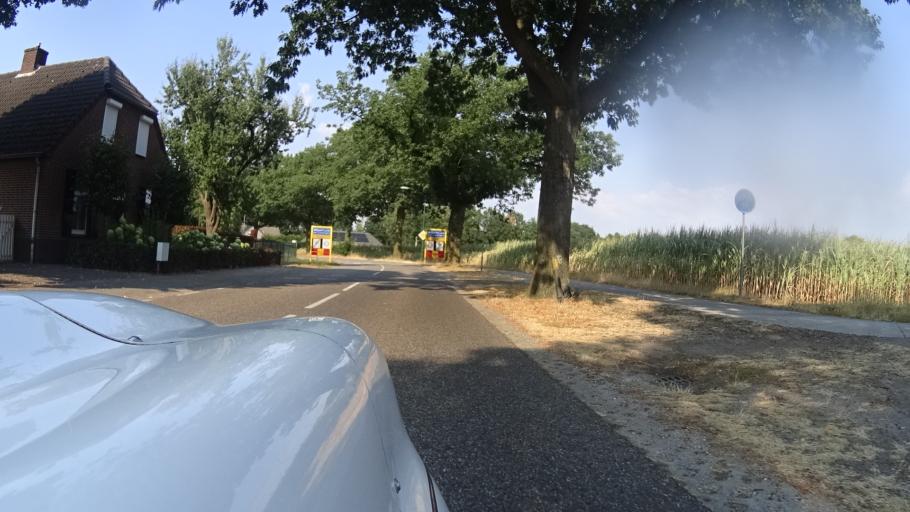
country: NL
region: North Brabant
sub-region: Gemeente Mill en Sint Hubert
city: Wilbertoord
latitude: 51.6599
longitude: 5.7714
